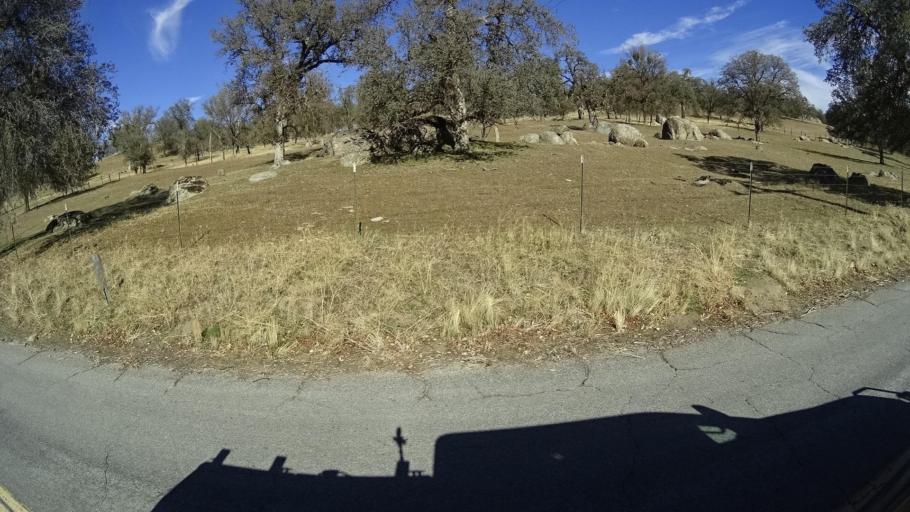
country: US
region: California
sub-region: Kern County
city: Alta Sierra
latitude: 35.6222
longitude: -118.7421
